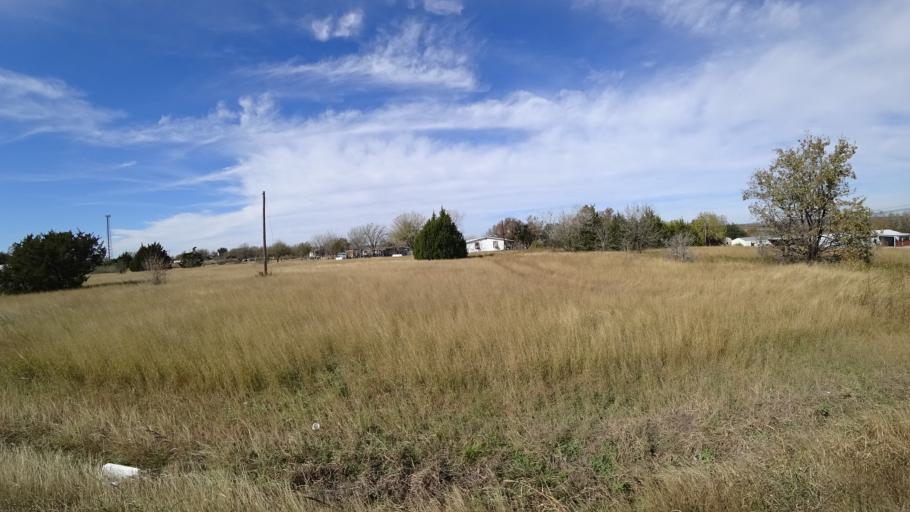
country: US
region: Texas
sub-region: Travis County
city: Onion Creek
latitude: 30.1162
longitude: -97.6993
